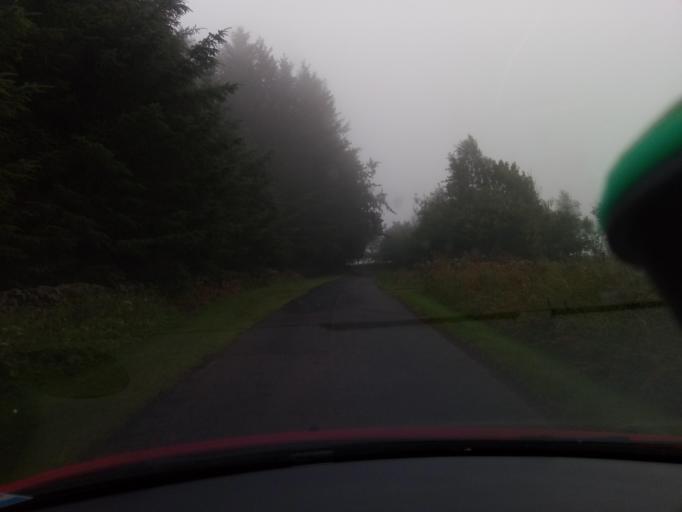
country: GB
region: Scotland
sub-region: The Scottish Borders
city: Melrose
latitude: 55.6488
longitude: -2.7418
